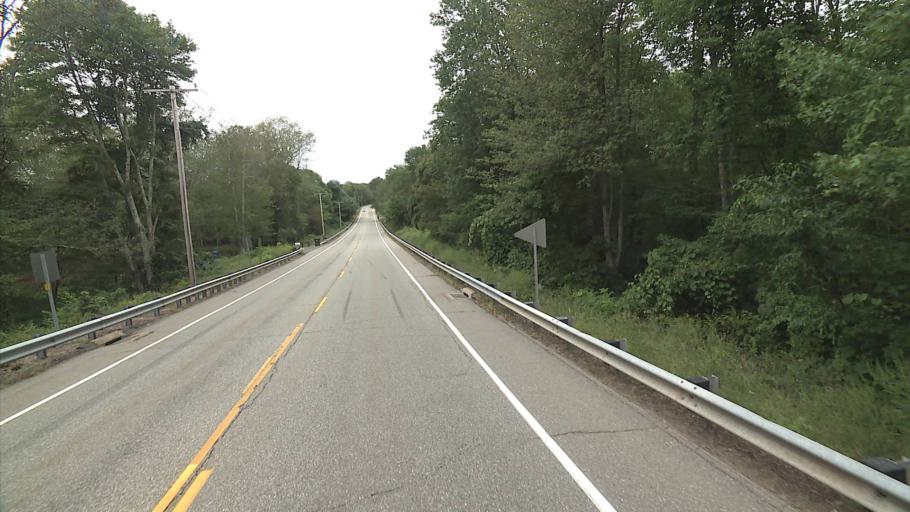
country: US
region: Connecticut
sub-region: Tolland County
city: Hebron
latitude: 41.6873
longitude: -72.4228
